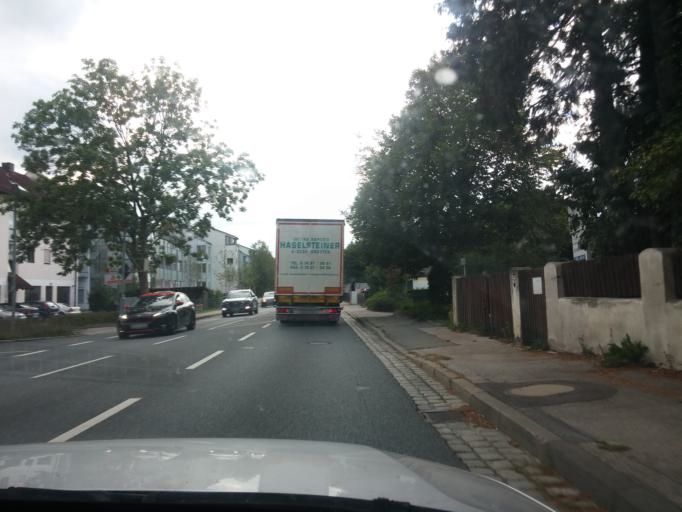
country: DE
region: Bavaria
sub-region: Upper Bavaria
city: Kirchseeon
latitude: 48.0749
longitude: 11.8873
